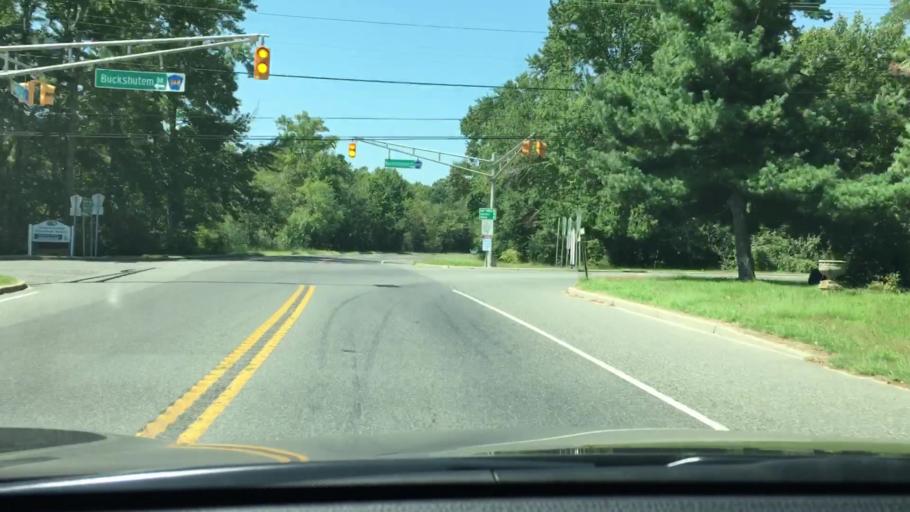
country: US
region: New Jersey
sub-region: Cumberland County
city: Port Norris
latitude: 39.2894
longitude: -74.9948
